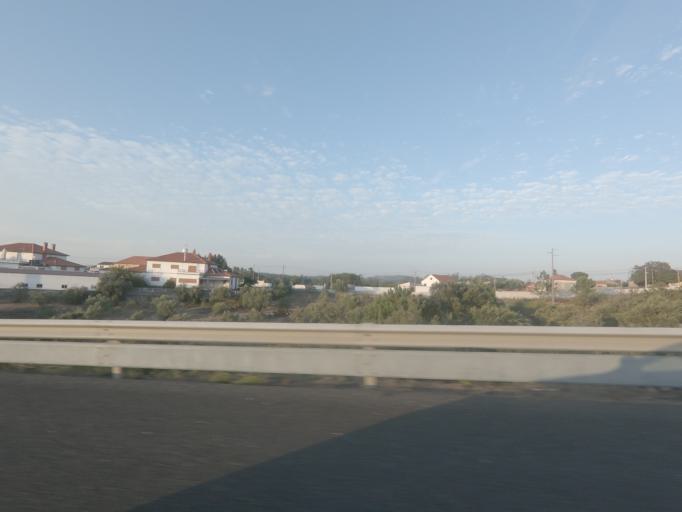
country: PT
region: Leiria
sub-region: Leiria
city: Santa Catarina da Serra
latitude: 39.7000
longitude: -8.6969
